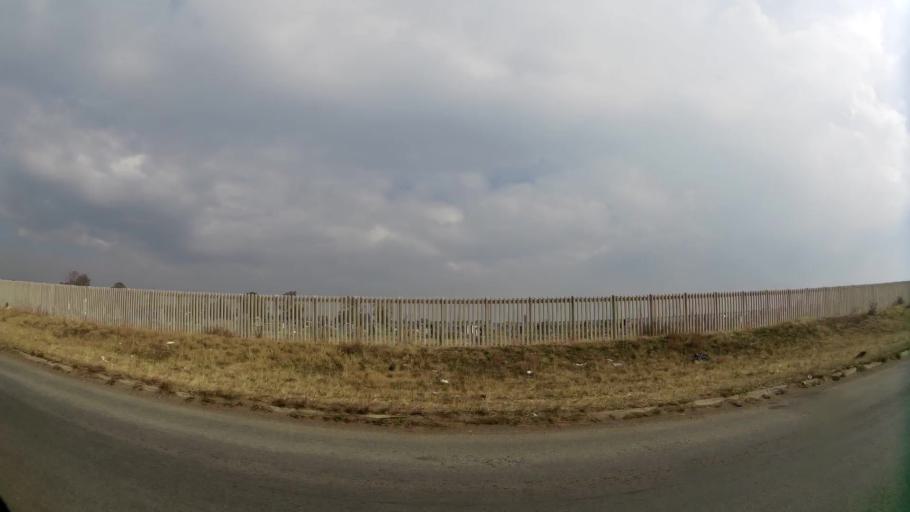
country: ZA
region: Gauteng
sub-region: Sedibeng District Municipality
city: Vanderbijlpark
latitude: -26.6887
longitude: 27.8604
